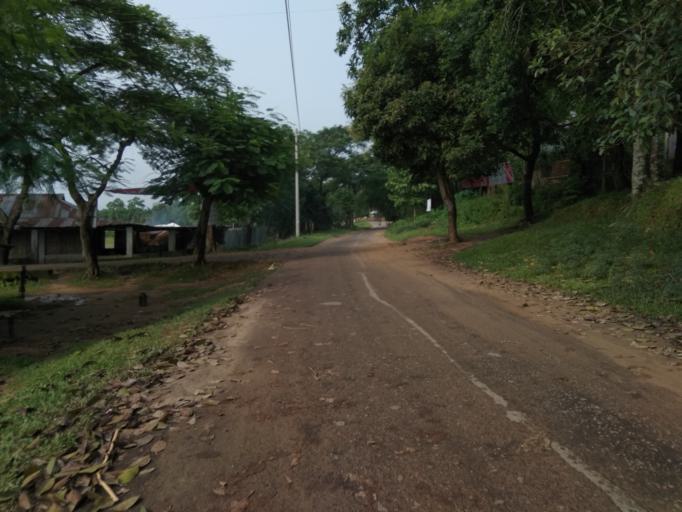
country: BD
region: Chittagong
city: Khagrachhari
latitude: 23.0212
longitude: 92.0150
